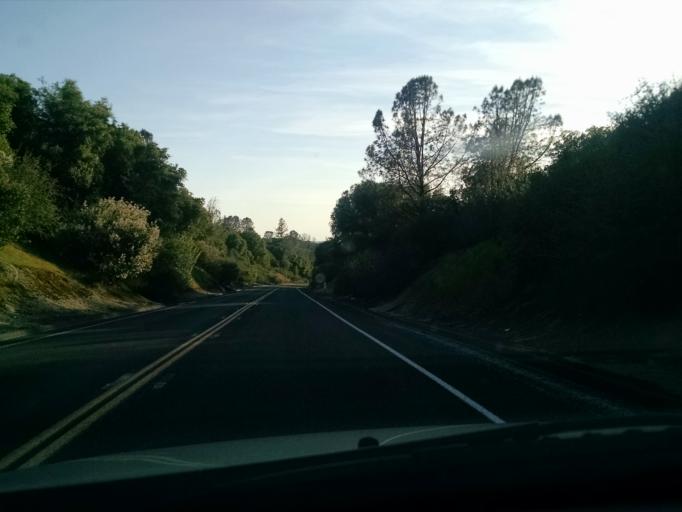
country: US
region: California
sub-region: Mariposa County
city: Midpines
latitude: 37.4507
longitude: -119.8300
